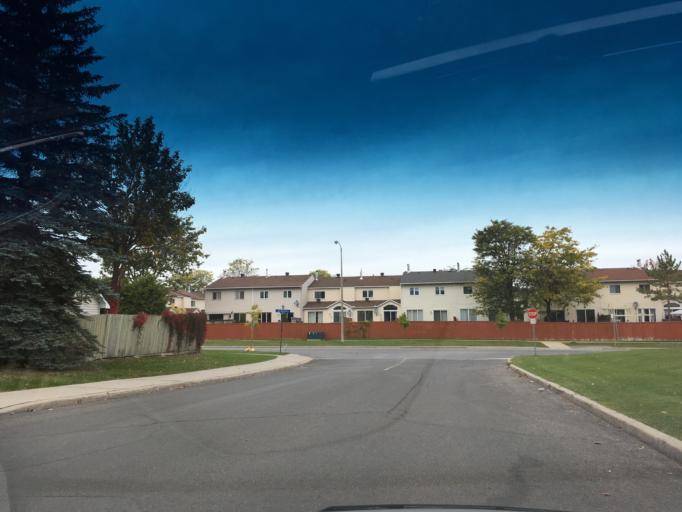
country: CA
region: Quebec
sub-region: Outaouais
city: Gatineau
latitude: 45.4613
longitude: -75.5061
